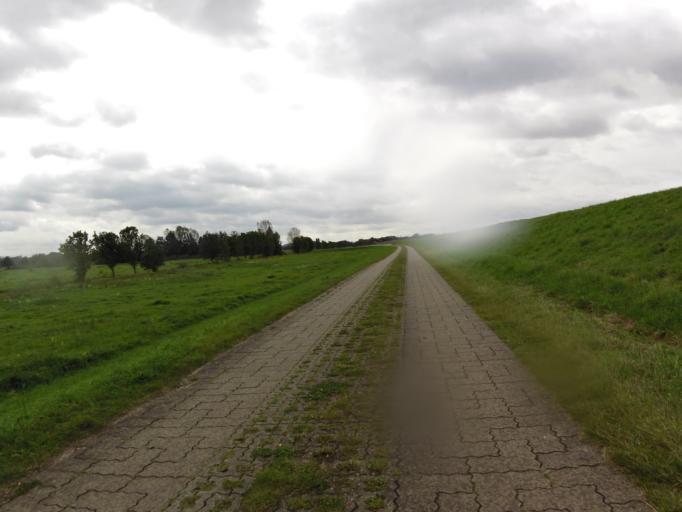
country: DE
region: Saxony-Anhalt
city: Havelberg
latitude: 52.8672
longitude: 12.0365
